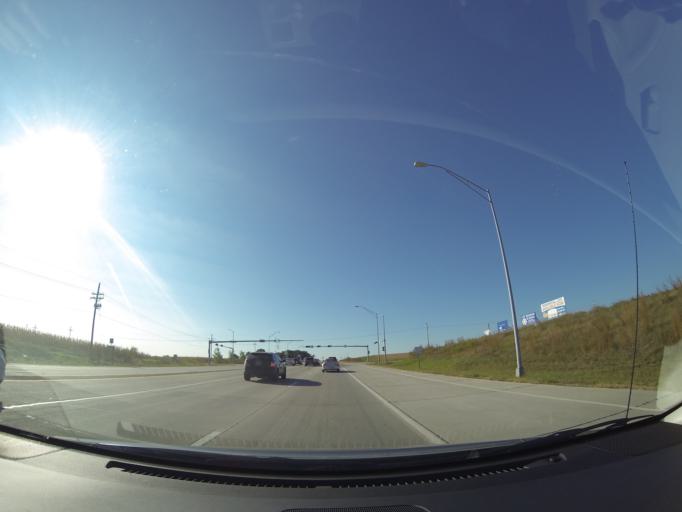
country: US
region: Nebraska
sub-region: Sarpy County
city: Gretna
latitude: 41.1912
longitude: -96.2344
